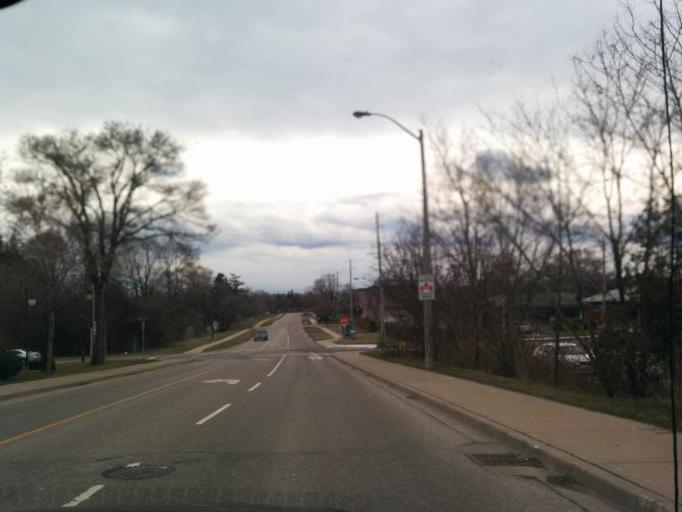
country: CA
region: Ontario
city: Etobicoke
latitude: 43.6239
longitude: -79.4928
